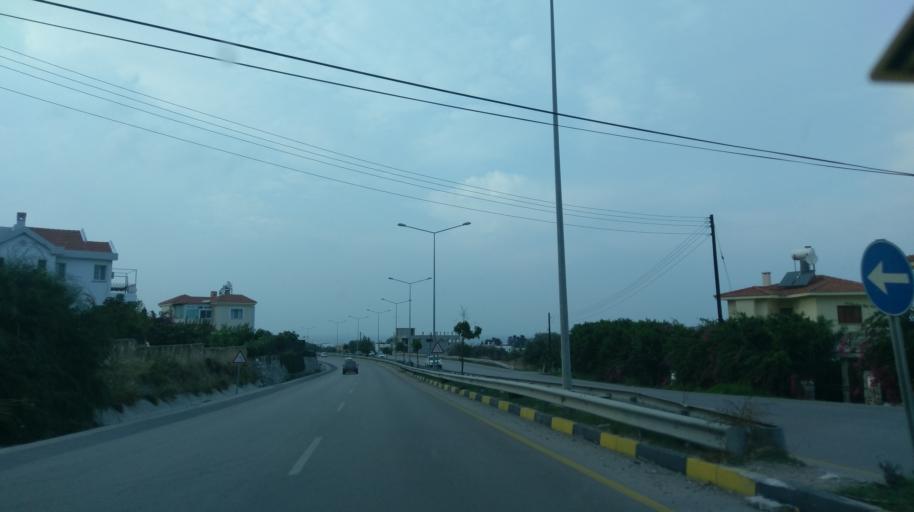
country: CY
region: Keryneia
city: Kyrenia
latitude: 35.3384
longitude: 33.2555
